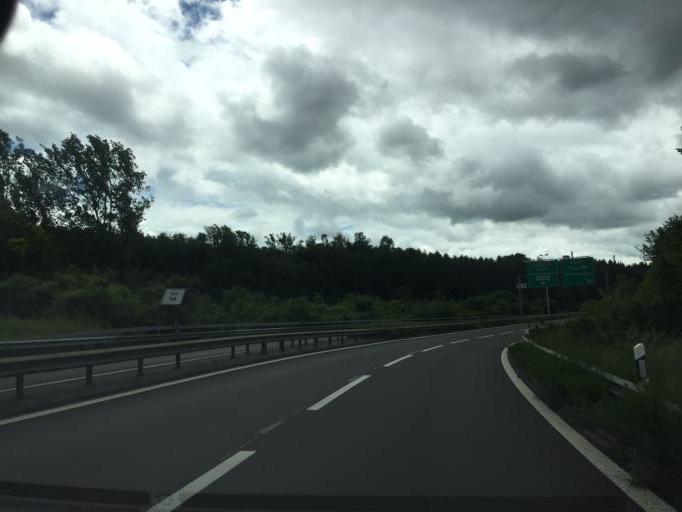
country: CH
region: Schaffhausen
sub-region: Bezirk Schaffhausen
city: Schaffhausen
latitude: 47.7155
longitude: 8.6536
